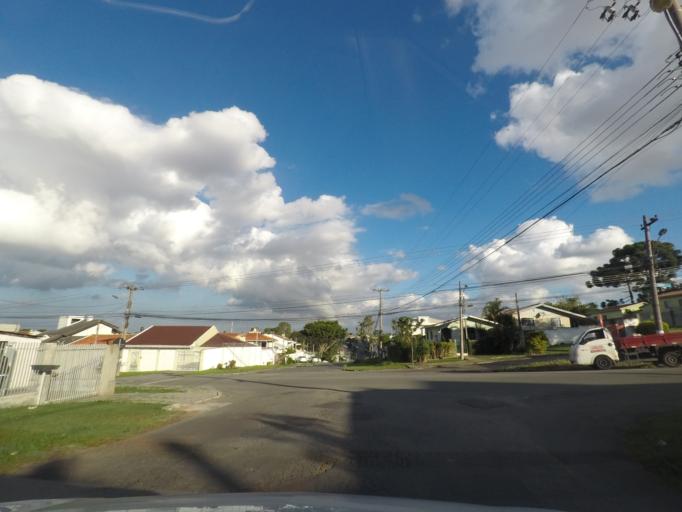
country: BR
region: Parana
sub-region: Sao Jose Dos Pinhais
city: Sao Jose dos Pinhais
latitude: -25.4933
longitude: -49.2569
